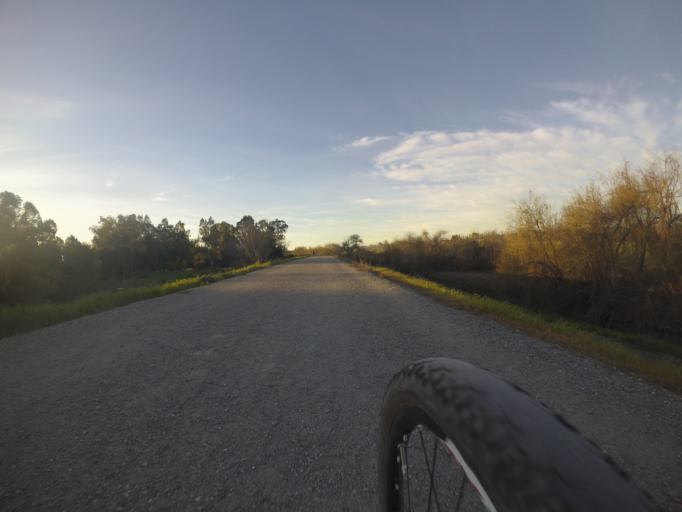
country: US
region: California
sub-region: Santa Clara County
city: Milpitas
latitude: 37.4065
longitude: -121.9541
